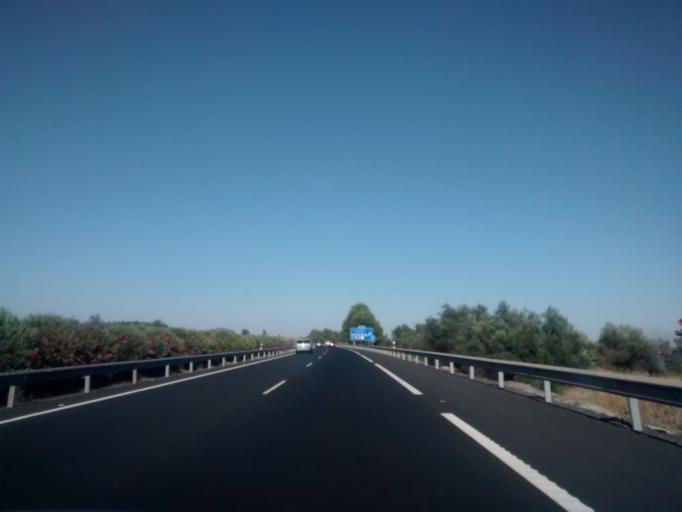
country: ES
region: Andalusia
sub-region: Provincia de Huelva
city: Manzanilla
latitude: 37.3450
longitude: -6.4365
